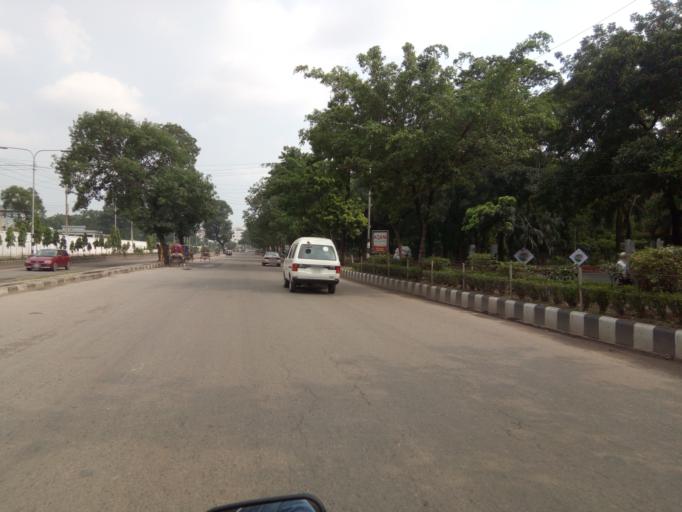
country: BD
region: Dhaka
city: Azimpur
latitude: 23.7689
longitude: 90.3828
